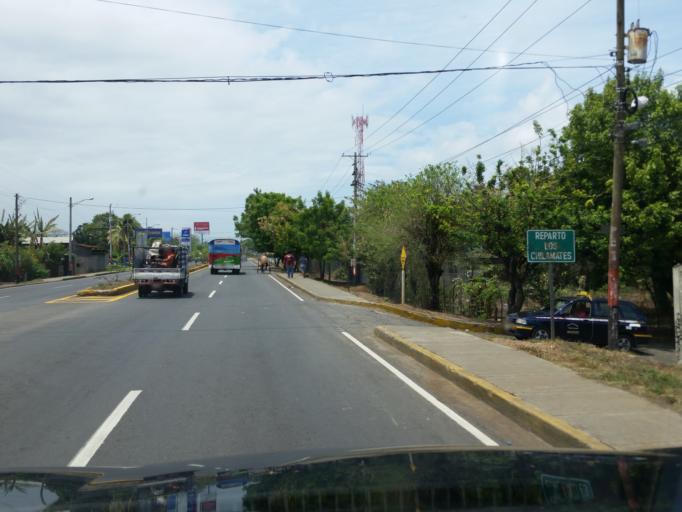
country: NI
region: Masaya
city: Masaya
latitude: 11.9899
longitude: -86.0992
